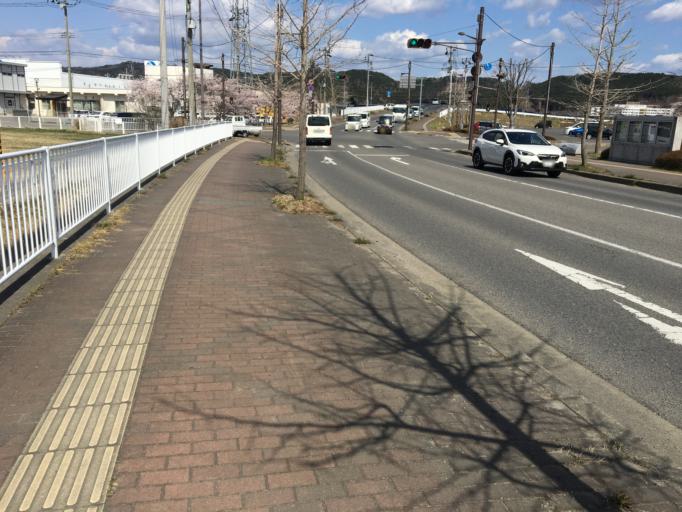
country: JP
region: Aomori
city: Hachinohe
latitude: 40.1911
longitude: 141.7777
